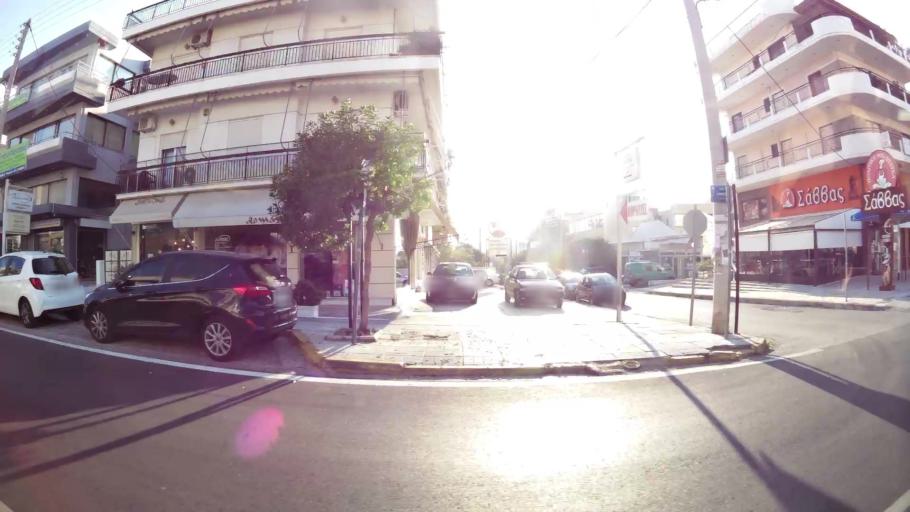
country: GR
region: Attica
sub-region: Nomarchia Athinas
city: Argyroupoli
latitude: 37.8934
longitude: 23.7638
